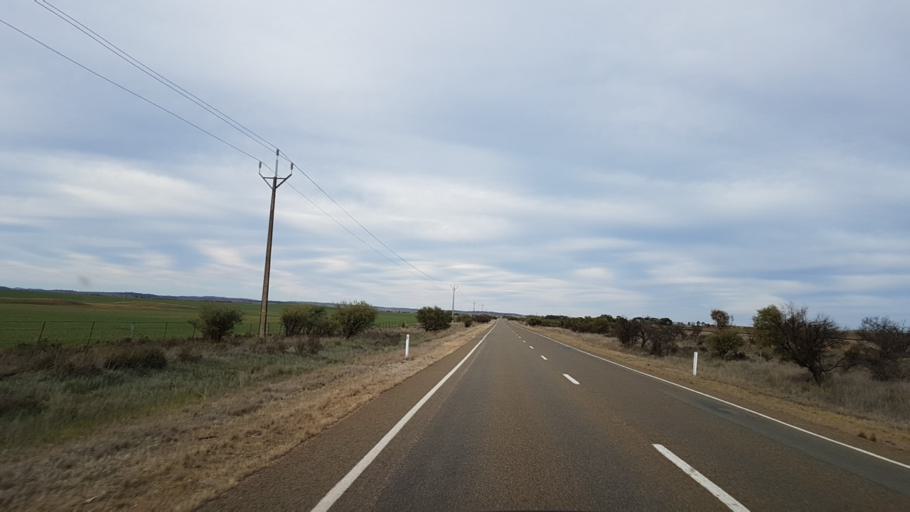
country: AU
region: South Australia
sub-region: Peterborough
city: Peterborough
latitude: -33.0075
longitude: 138.7690
